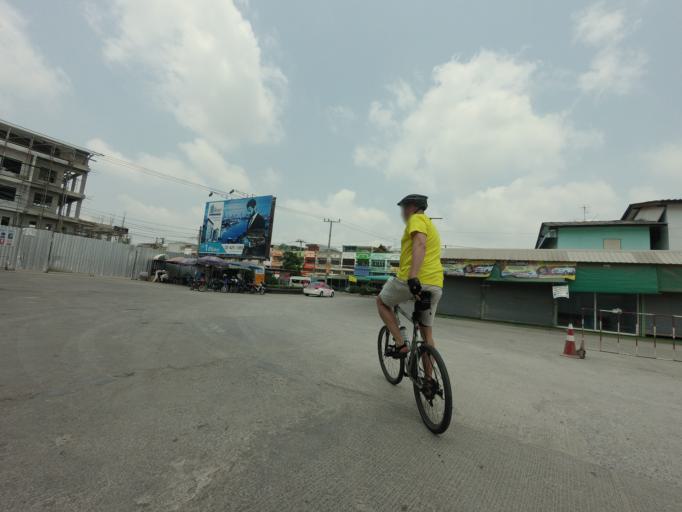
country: TH
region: Samut Prakan
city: Samut Prakan
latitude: 13.5981
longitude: 100.5854
